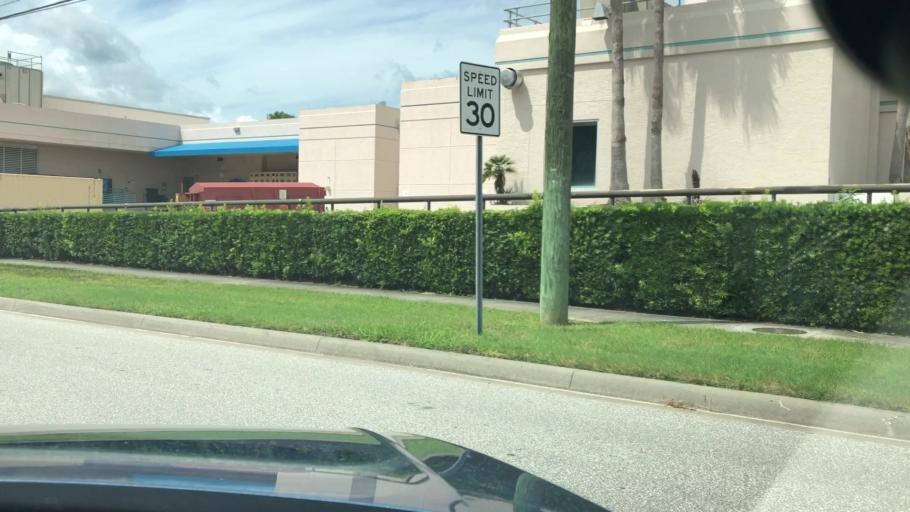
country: US
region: Florida
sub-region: Volusia County
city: New Smyrna Beach
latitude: 29.0212
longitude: -80.9217
